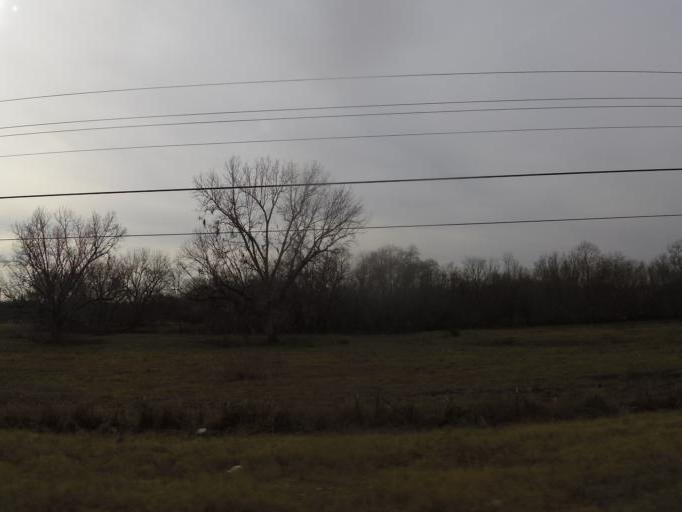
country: US
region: Alabama
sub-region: Montgomery County
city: Pike Road
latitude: 32.3002
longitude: -86.2031
